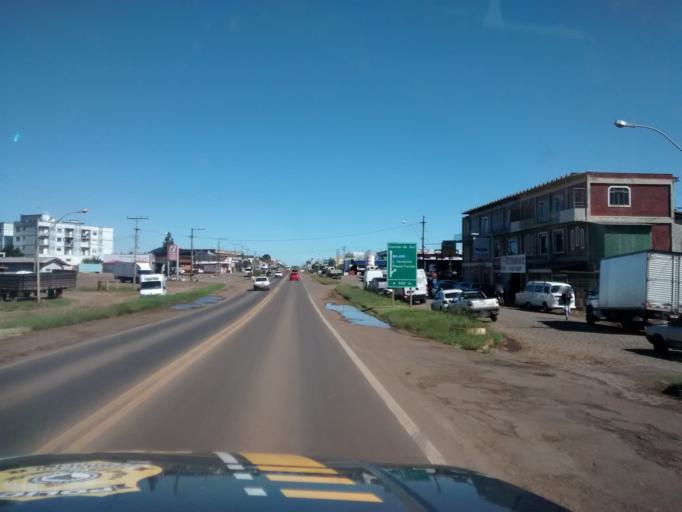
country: BR
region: Rio Grande do Sul
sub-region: Vacaria
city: Vacaria
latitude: -28.5059
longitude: -50.9257
